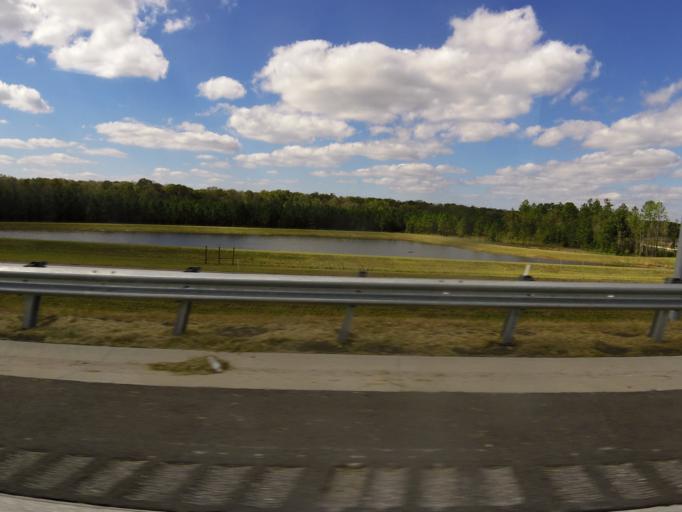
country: US
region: Florida
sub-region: Saint Johns County
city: Fruit Cove
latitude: 30.0891
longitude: -81.5203
